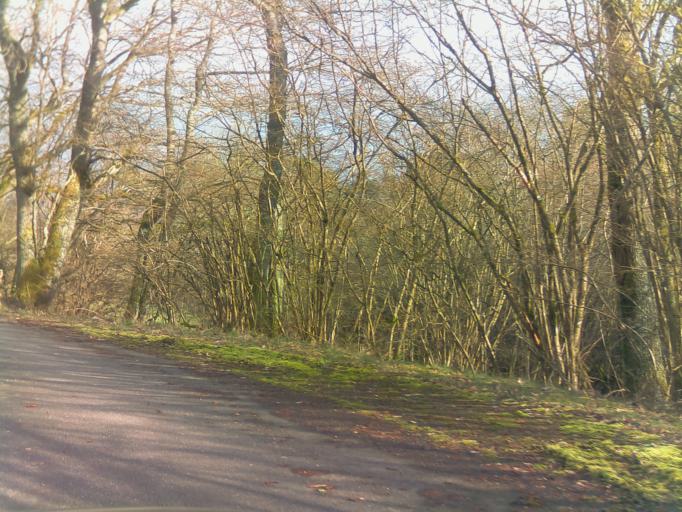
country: DE
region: Rheinland-Pfalz
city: Kronweiler
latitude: 49.6530
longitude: 7.2706
